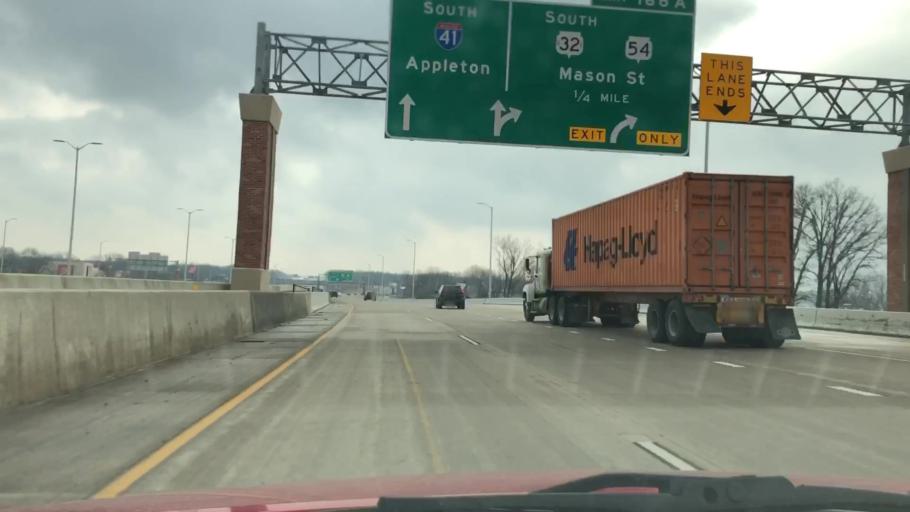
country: US
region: Wisconsin
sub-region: Brown County
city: Howard
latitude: 44.5314
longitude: -88.0818
